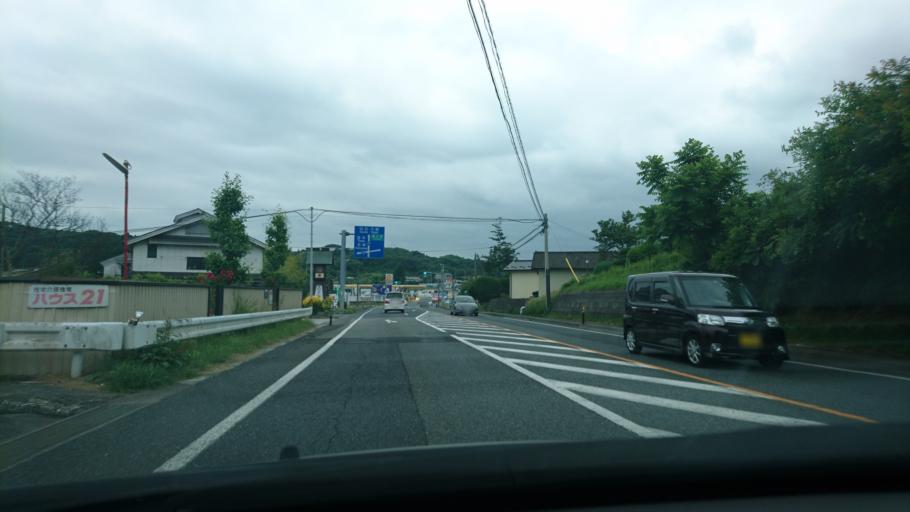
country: JP
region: Miyagi
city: Furukawa
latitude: 38.7145
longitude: 141.0212
